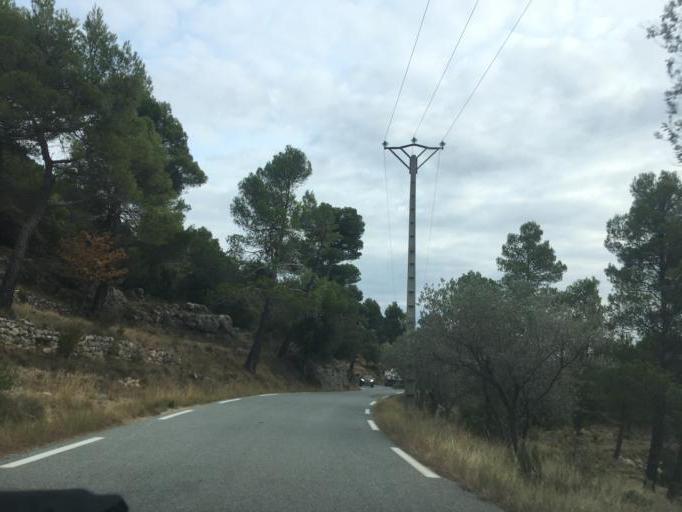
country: FR
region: Provence-Alpes-Cote d'Azur
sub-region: Departement du Var
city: Villecroze
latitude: 43.5764
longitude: 6.3167
